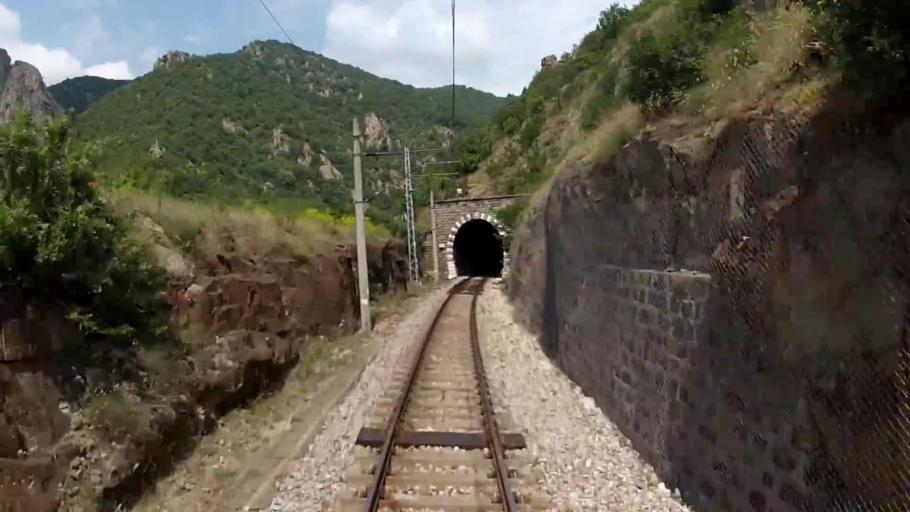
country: BG
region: Blagoevgrad
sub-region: Obshtina Kresna
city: Stara Kresna
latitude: 41.8023
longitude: 23.1625
